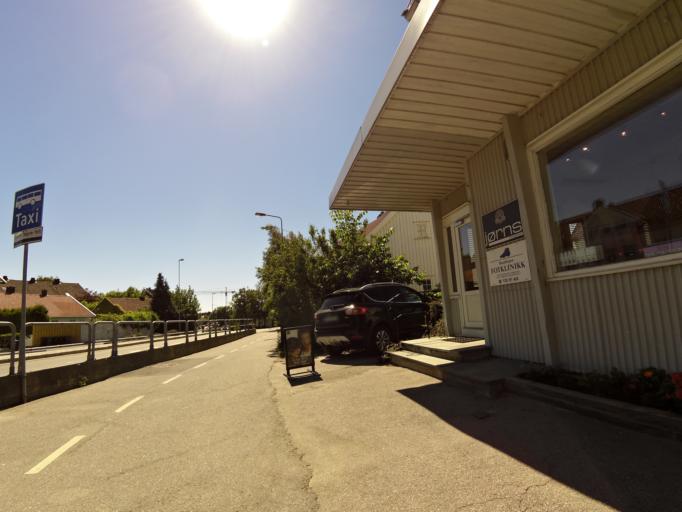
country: NO
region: Vest-Agder
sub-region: Kristiansand
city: Kristiansand
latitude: 58.1517
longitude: 8.0079
